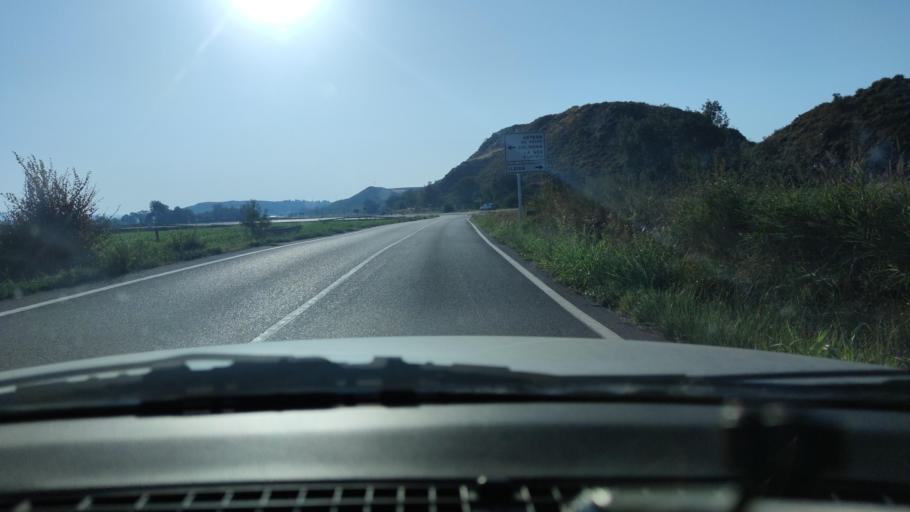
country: ES
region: Catalonia
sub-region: Provincia de Lleida
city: Balaguer
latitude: 41.8021
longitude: 0.8430
